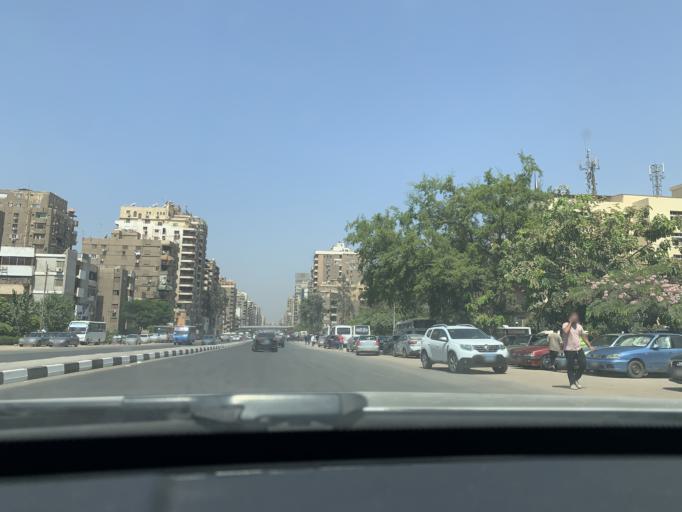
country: EG
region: Muhafazat al Qahirah
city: Cairo
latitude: 30.0496
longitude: 31.3470
